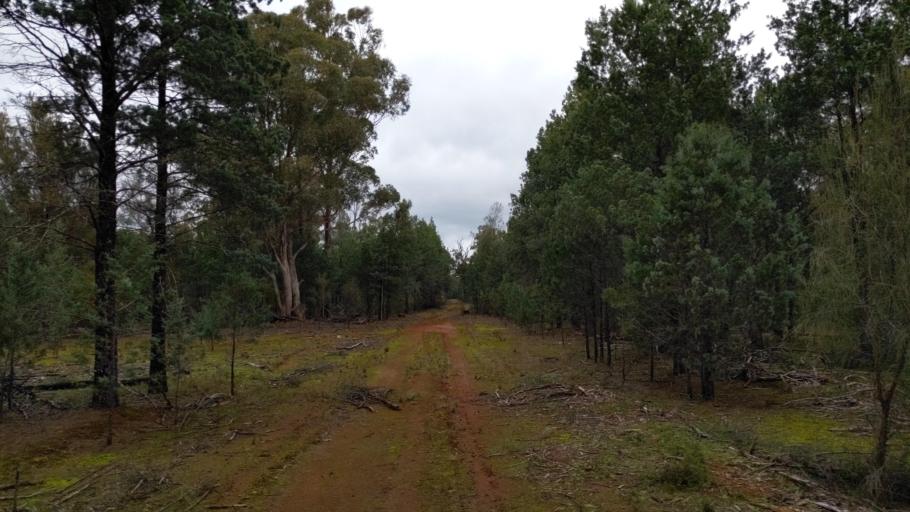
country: AU
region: New South Wales
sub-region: Coolamon
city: Coolamon
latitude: -34.8435
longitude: 146.9331
